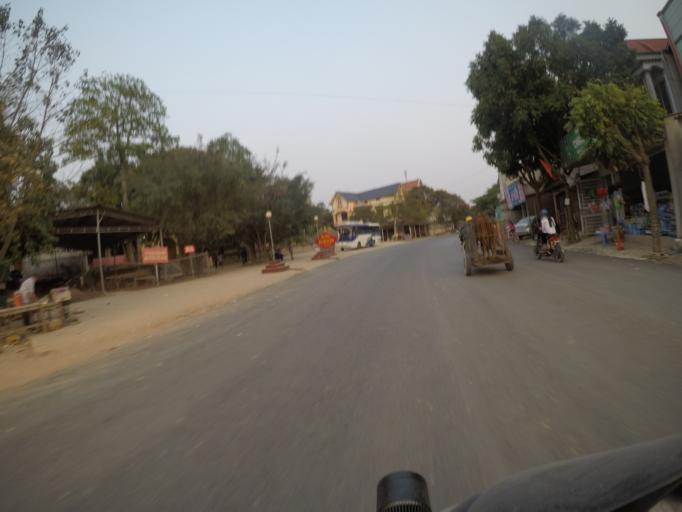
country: VN
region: Vinh Phuc
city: Trai Ngau
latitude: 21.4402
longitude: 105.5729
